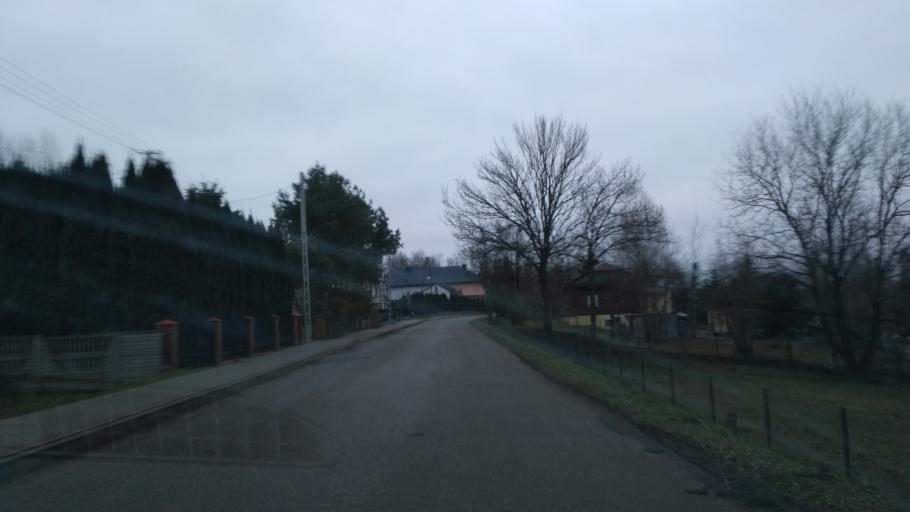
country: PL
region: Subcarpathian Voivodeship
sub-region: Powiat przeworski
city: Zarzecze
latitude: 49.9354
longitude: 22.5714
